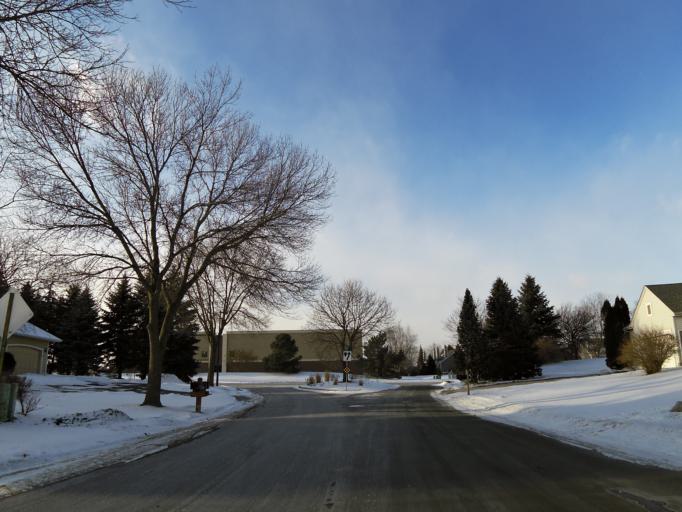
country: US
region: Minnesota
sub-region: Washington County
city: Woodbury
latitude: 44.9378
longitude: -92.9295
